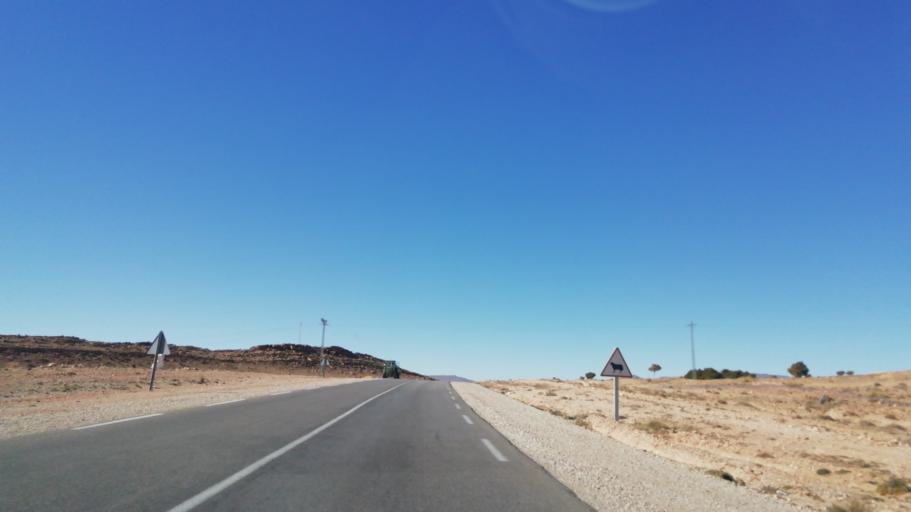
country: DZ
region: El Bayadh
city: El Bayadh
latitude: 33.6096
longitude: 1.2370
